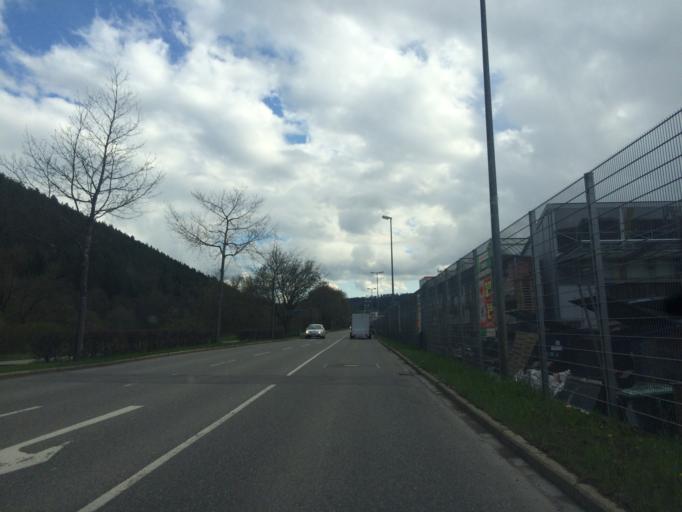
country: DE
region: Baden-Wuerttemberg
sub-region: Freiburg Region
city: Tuttlingen
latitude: 47.9966
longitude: 8.8310
